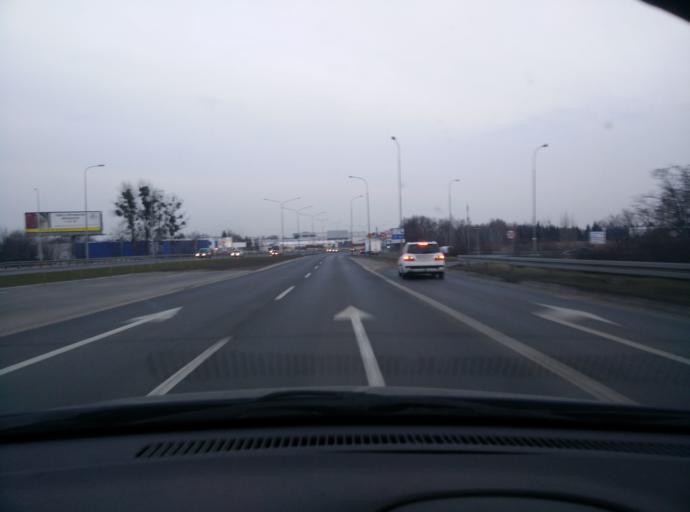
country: PL
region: Greater Poland Voivodeship
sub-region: Poznan
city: Poznan
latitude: 52.3701
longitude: 16.9894
